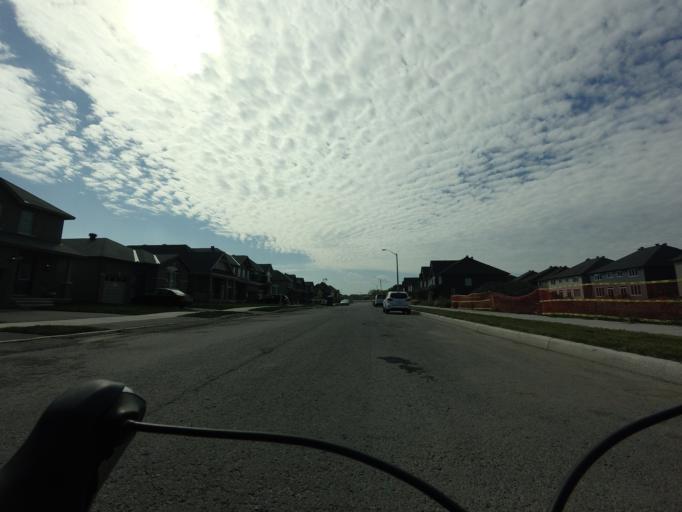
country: CA
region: Ontario
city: Bells Corners
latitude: 45.2740
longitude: -75.7802
